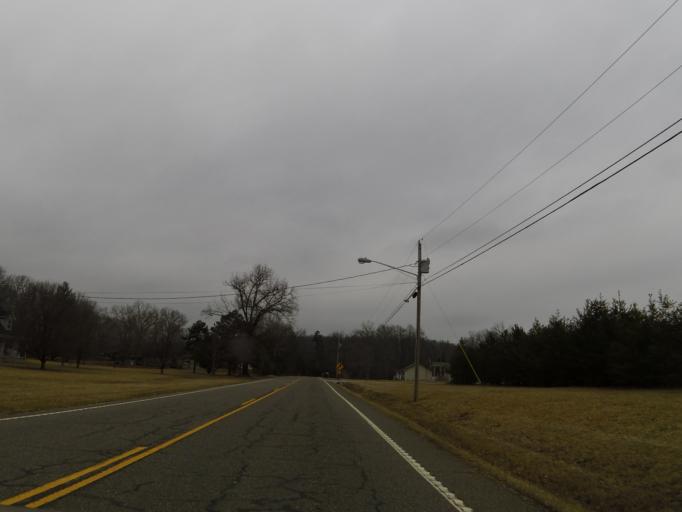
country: US
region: Tennessee
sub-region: Morgan County
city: Wartburg
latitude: 36.2661
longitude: -84.6607
